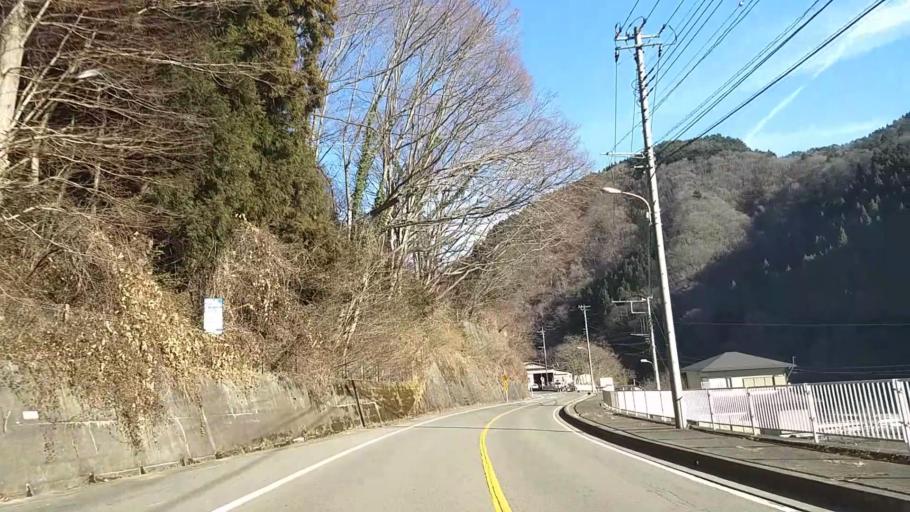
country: JP
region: Yamanashi
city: Otsuki
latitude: 35.5140
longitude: 139.0095
